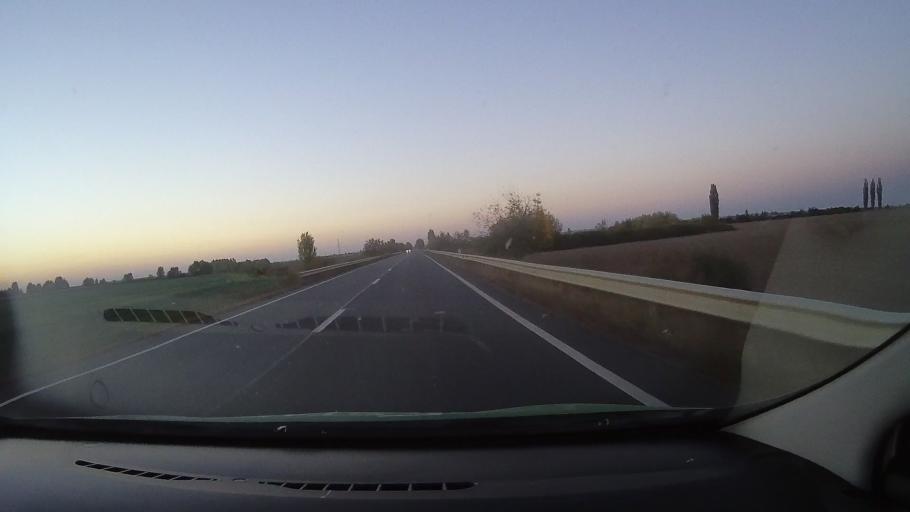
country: RO
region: Bihor
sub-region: Comuna Valea lui Mihai
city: Valea lui Mihai
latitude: 47.4885
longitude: 22.1569
